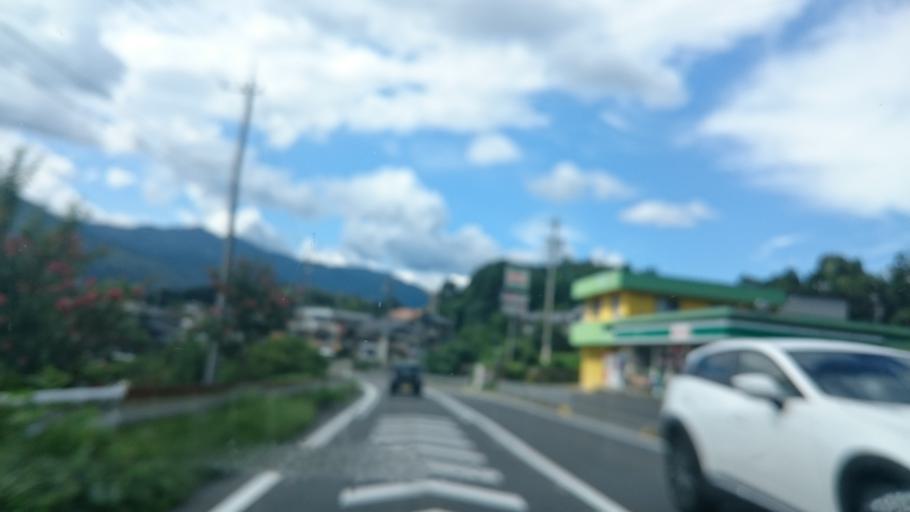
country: JP
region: Gifu
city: Nakatsugawa
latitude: 35.5327
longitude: 137.4547
